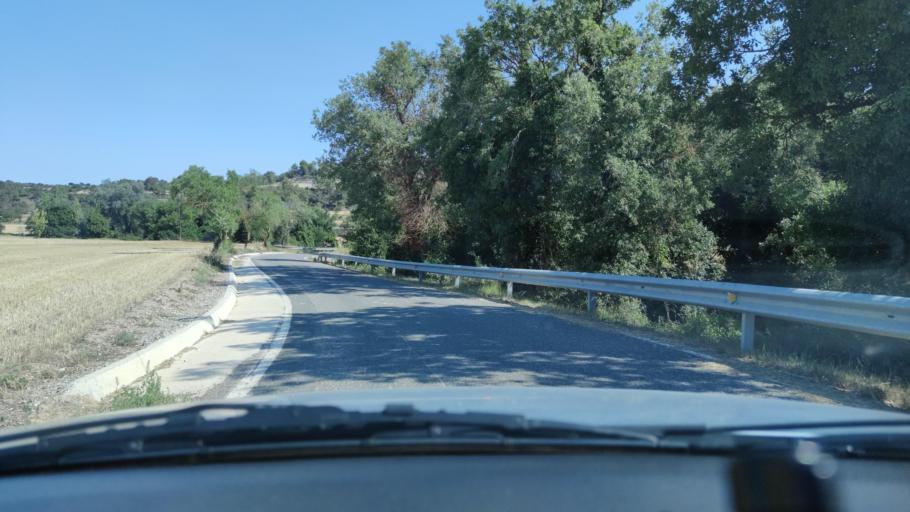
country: ES
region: Catalonia
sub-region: Provincia de Lleida
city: Sant Guim de Freixenet
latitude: 41.6652
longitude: 1.3694
